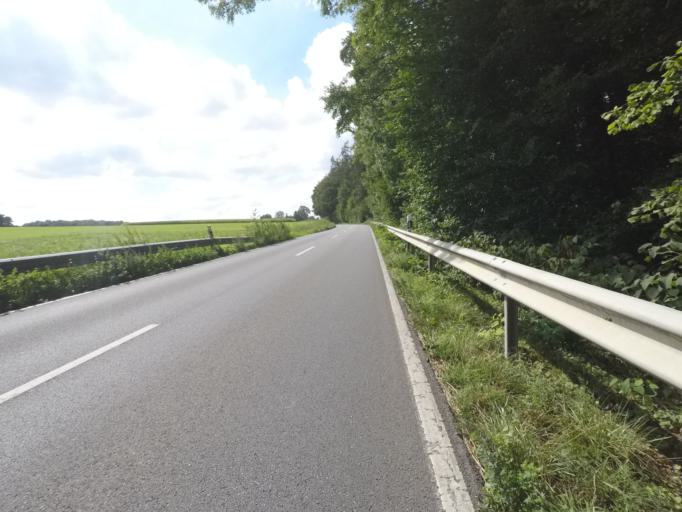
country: DE
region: North Rhine-Westphalia
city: Spenge
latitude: 52.0820
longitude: 8.4821
